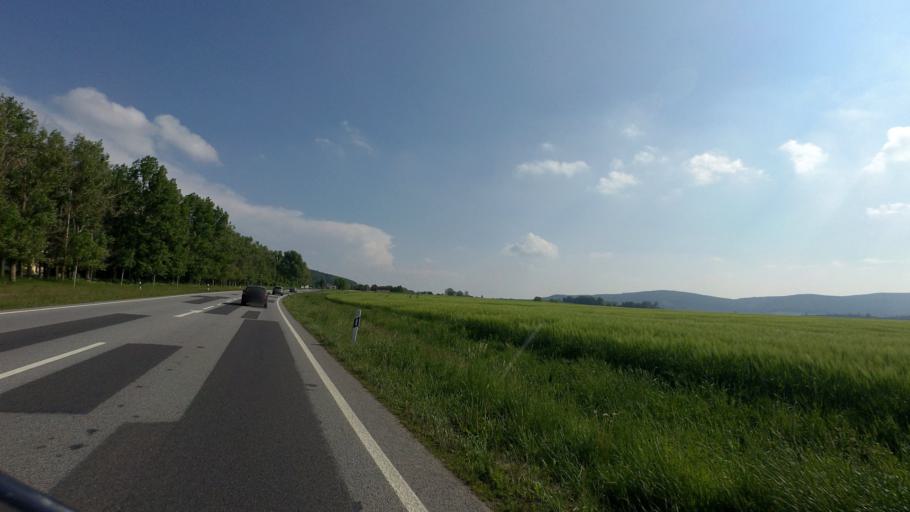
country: DE
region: Saxony
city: Grosspostwitz
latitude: 51.1468
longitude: 14.4390
